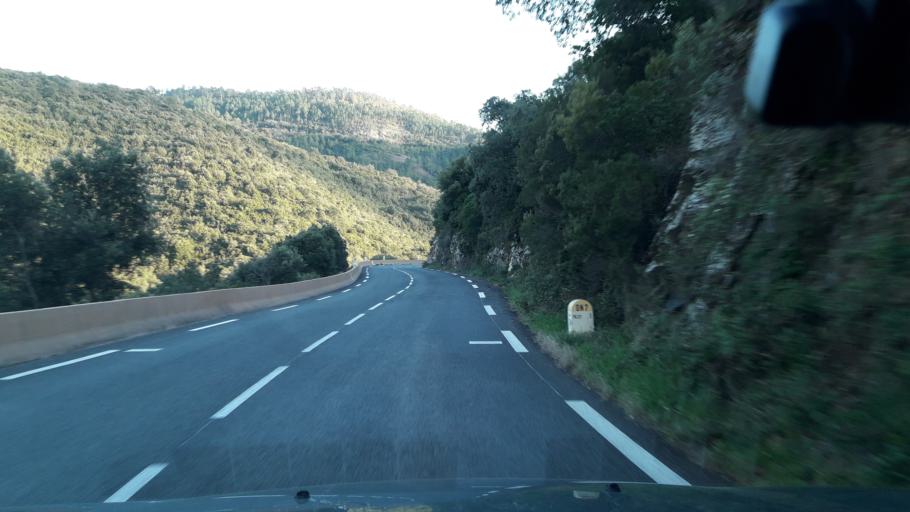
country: FR
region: Provence-Alpes-Cote d'Azur
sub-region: Departement du Var
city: Saint-Raphael
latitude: 43.4907
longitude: 6.7790
